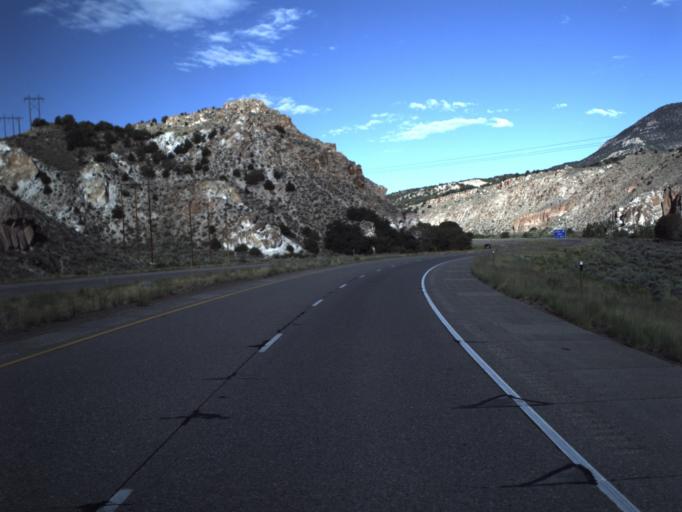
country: US
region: Utah
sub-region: Sevier County
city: Monroe
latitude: 38.5777
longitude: -112.3205
